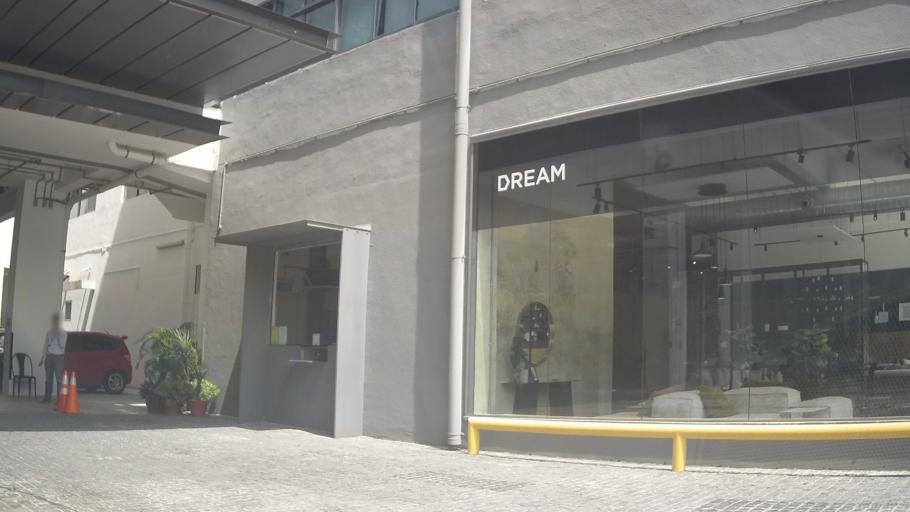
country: SG
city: Singapore
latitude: 1.3123
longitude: 103.8645
